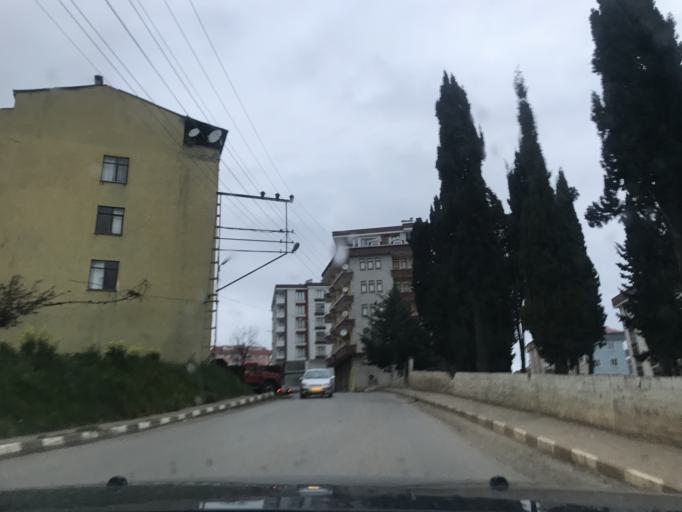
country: TR
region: Trabzon
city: Akcaabat
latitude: 41.0124
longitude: 39.5896
